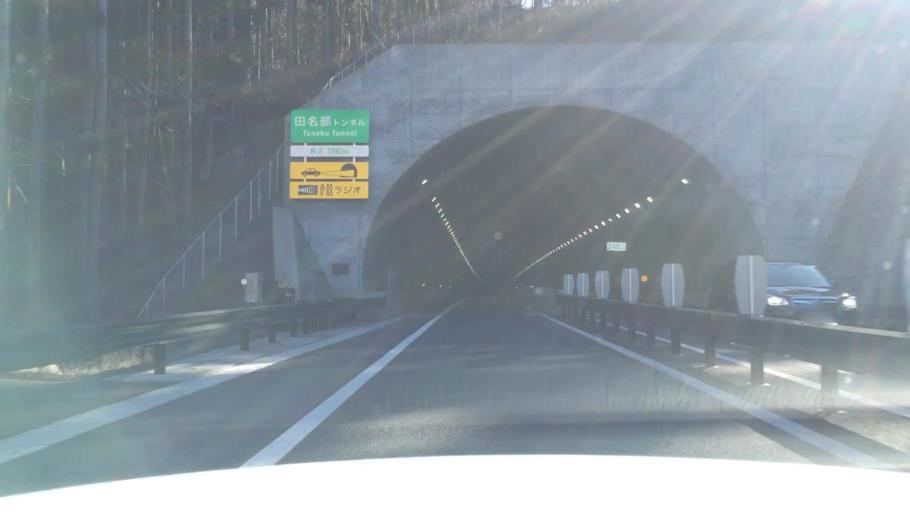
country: JP
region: Iwate
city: Yamada
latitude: 39.5145
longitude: 141.9438
